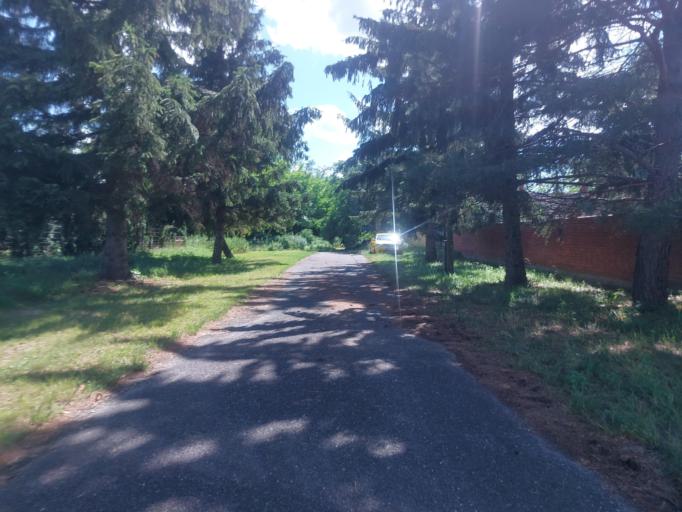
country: HU
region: Veszprem
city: Devecser
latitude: 47.1911
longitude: 17.3513
